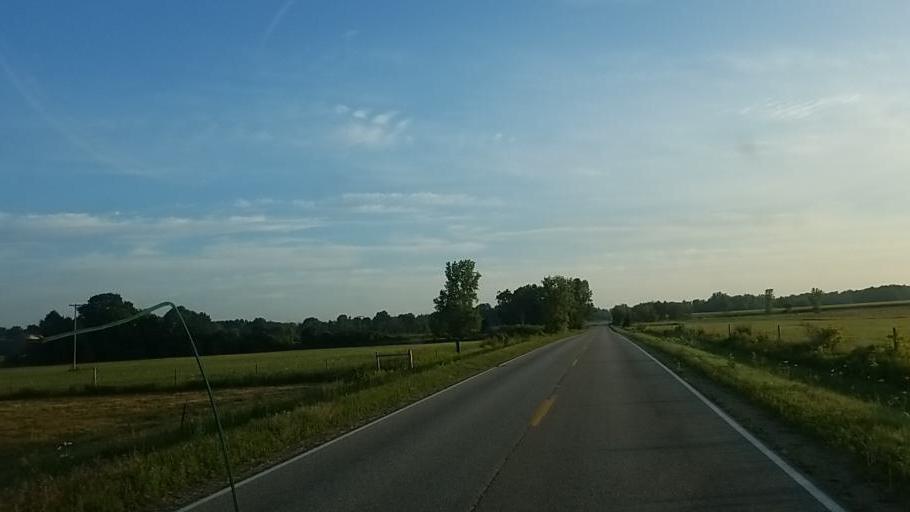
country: US
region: Michigan
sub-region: Montcalm County
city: Howard City
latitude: 43.3400
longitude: -85.4031
